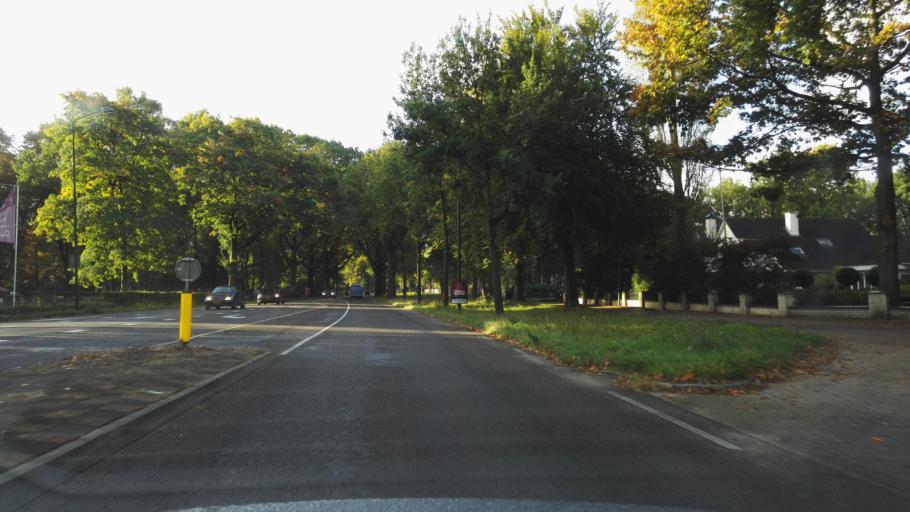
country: NL
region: Gelderland
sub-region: Gemeente Apeldoorn
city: Beekbergen
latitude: 52.1845
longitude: 5.9620
